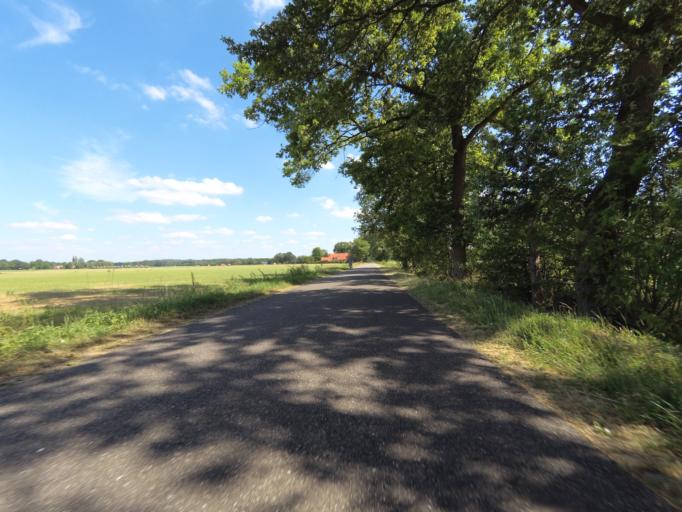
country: NL
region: Overijssel
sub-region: Gemeente Oldenzaal
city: Oldenzaal
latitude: 52.3349
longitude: 6.9131
